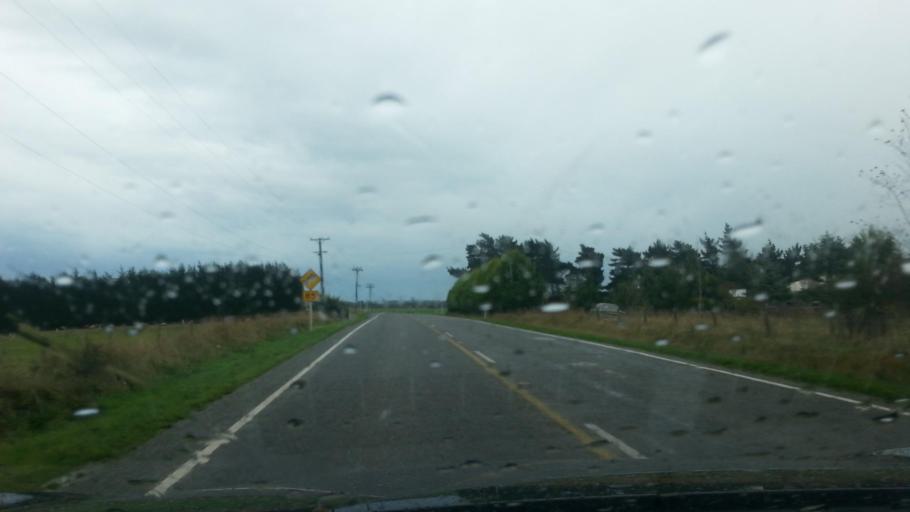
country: NZ
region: Southland
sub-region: Invercargill City
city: Invercargill
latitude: -46.3487
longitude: 168.3872
